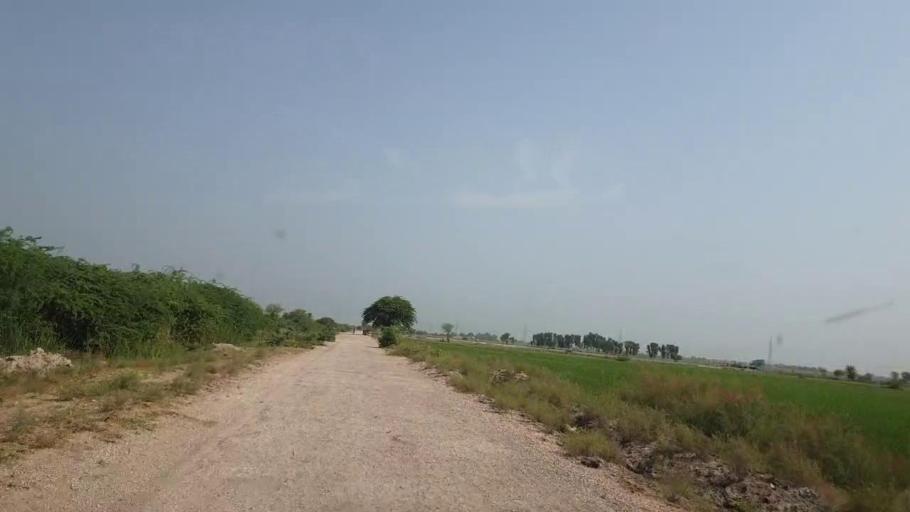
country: PK
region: Sindh
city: Lakhi
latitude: 27.8240
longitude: 68.6884
